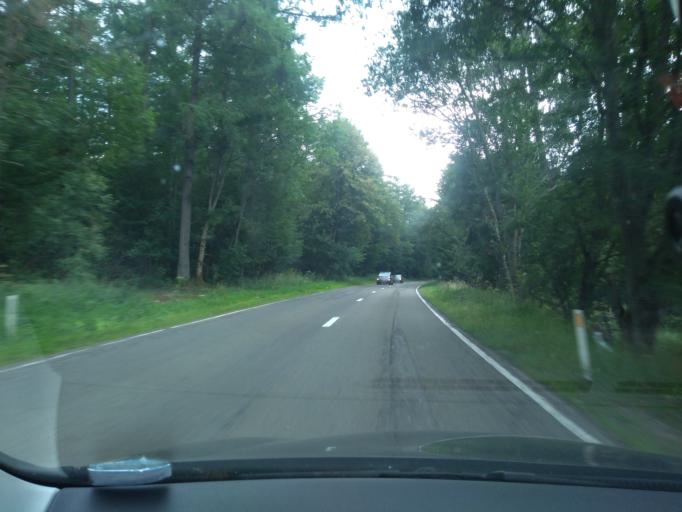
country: BE
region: Wallonia
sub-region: Province du Luxembourg
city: Sainte-Ode
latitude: 50.0219
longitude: 5.5057
